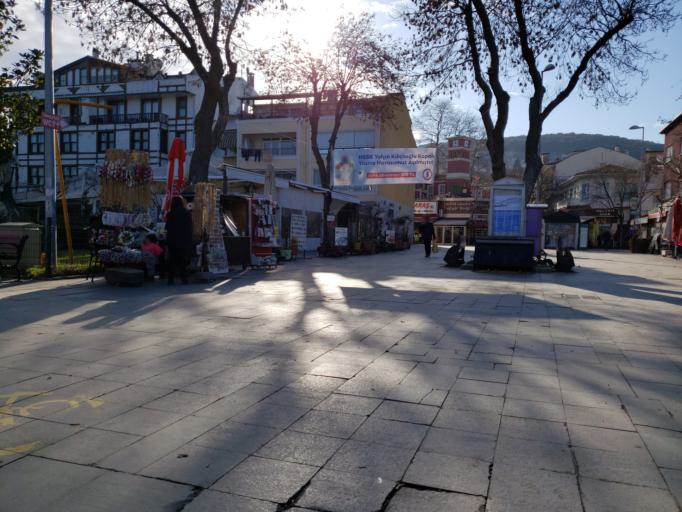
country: TR
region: Istanbul
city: Adalan
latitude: 40.8779
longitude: 29.1006
